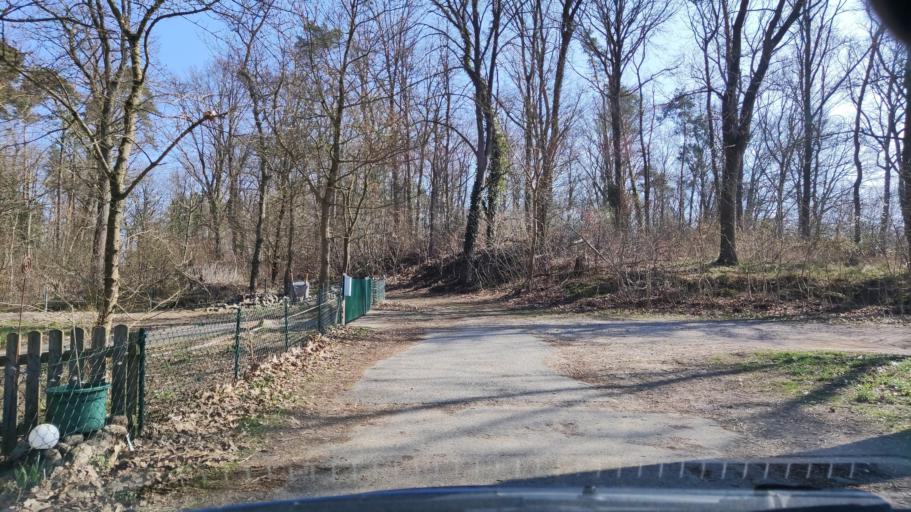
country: DE
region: Lower Saxony
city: Clenze
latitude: 52.9397
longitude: 10.9634
